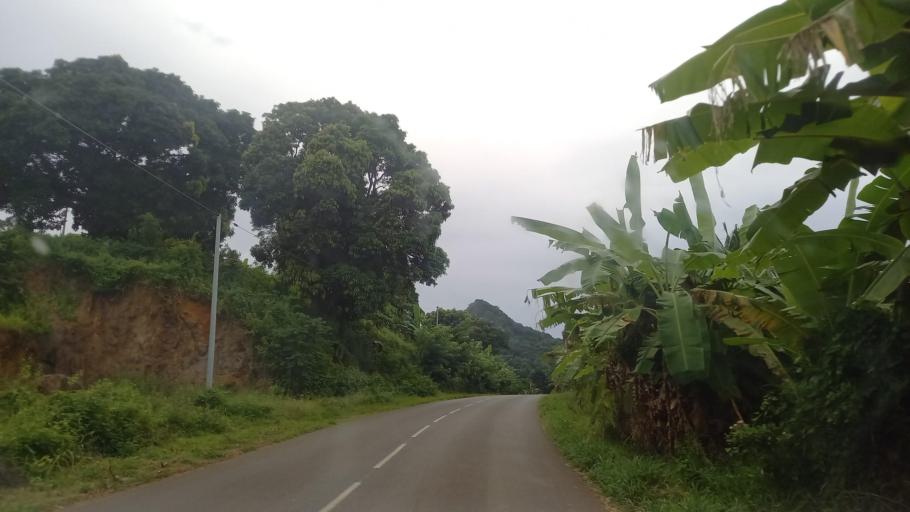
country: YT
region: Kani-Keli
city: Kani Keli
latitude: -12.9226
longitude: 45.1041
